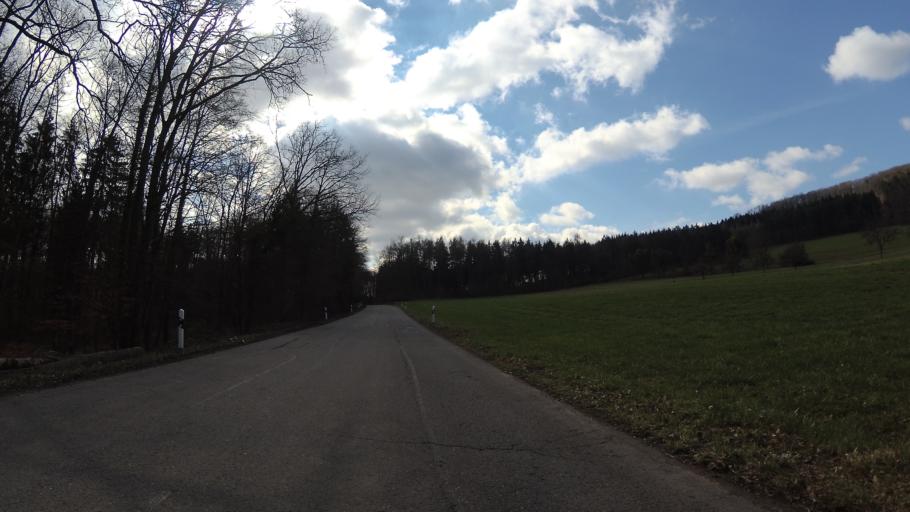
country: DE
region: Saarland
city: Rehlingen-Siersburg
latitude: 49.3905
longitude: 6.6599
